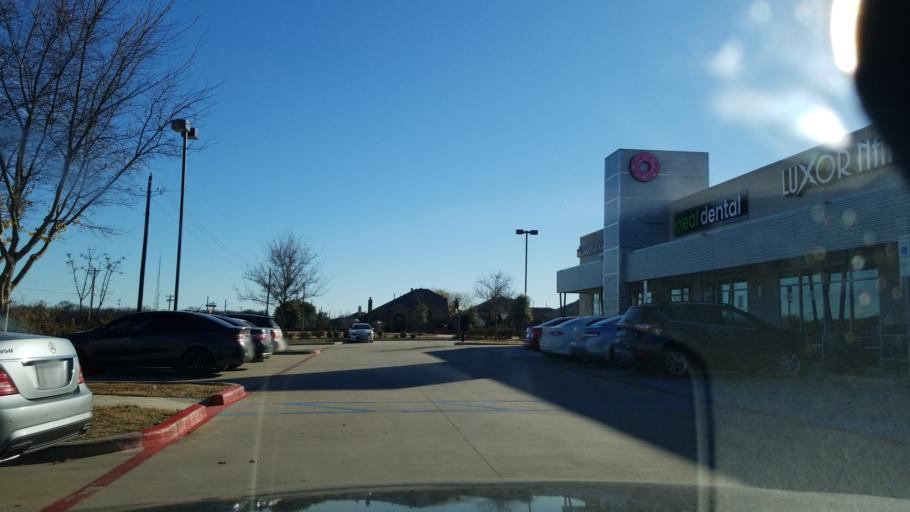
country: US
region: Texas
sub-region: Denton County
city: Corinth
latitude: 33.1443
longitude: -97.1056
